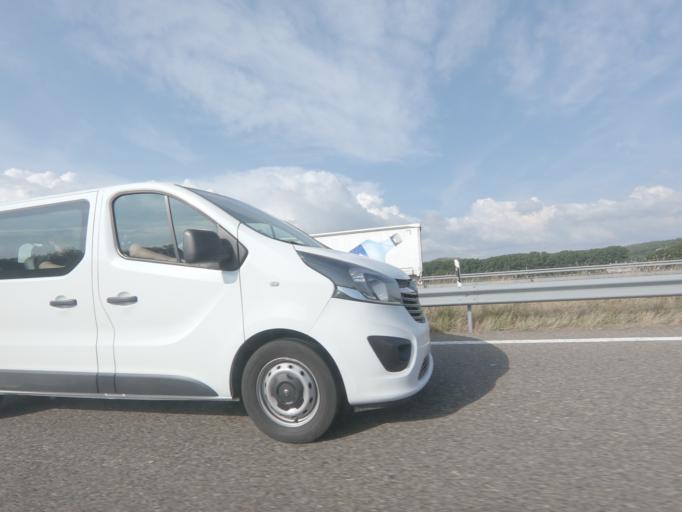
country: ES
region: Galicia
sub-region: Provincia de Ourense
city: Xinzo de Limia
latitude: 42.0760
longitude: -7.7091
